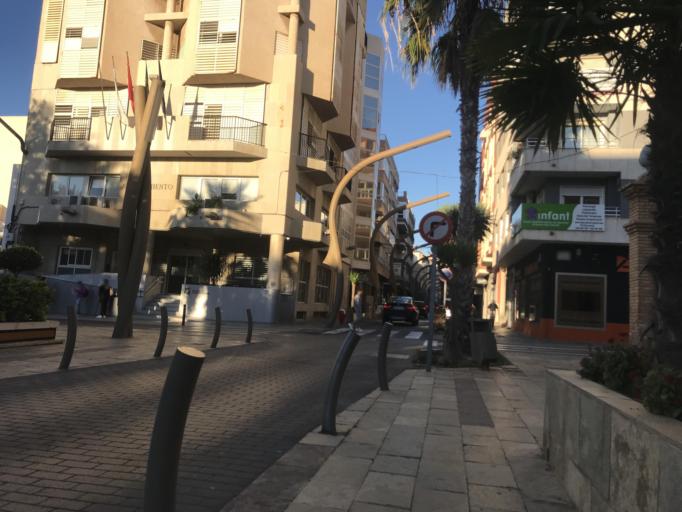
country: ES
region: Valencia
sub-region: Provincia de Alicante
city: Torrevieja
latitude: 37.9778
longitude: -0.6830
